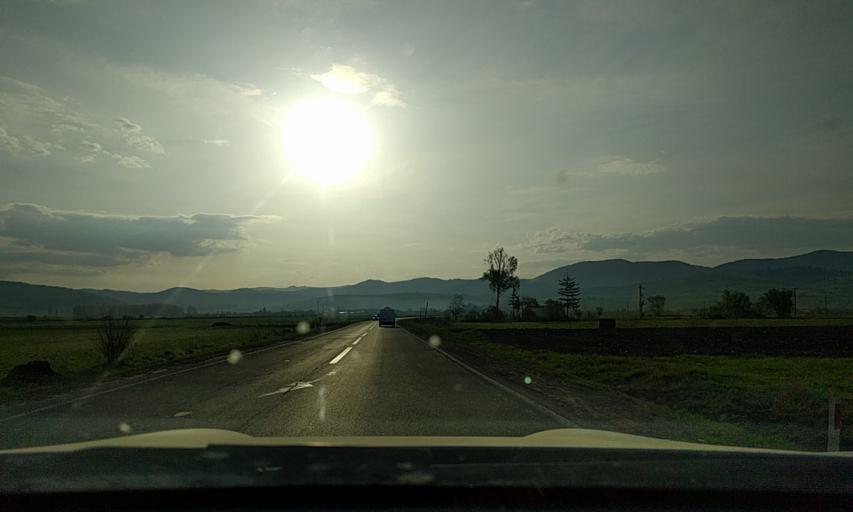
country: RO
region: Covasna
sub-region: Comuna Lemnia
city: Lemnia
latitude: 46.0436
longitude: 26.2758
